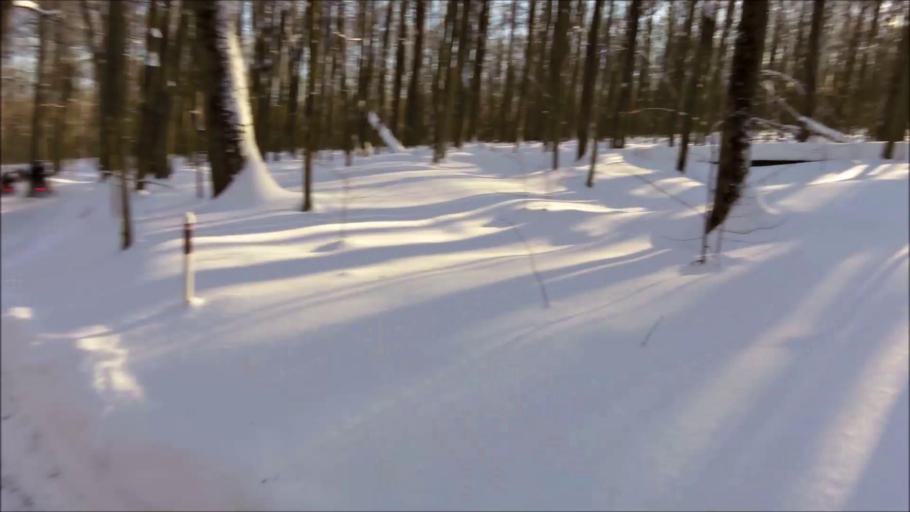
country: US
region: New York
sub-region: Chautauqua County
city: Mayville
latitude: 42.2752
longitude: -79.3888
